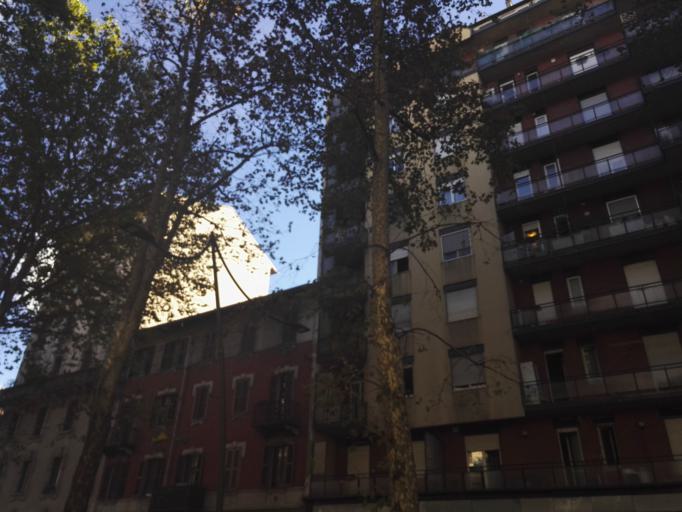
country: IT
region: Lombardy
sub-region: Citta metropolitana di Milano
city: Milano
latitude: 45.4433
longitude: 9.2166
